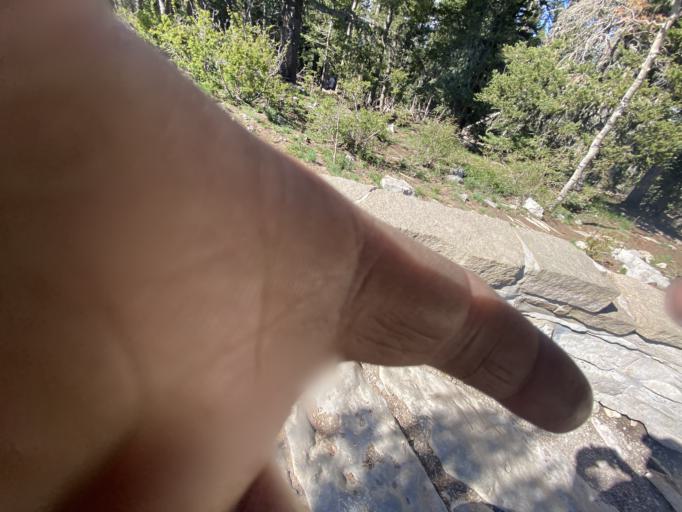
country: US
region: New Mexico
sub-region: Bernalillo County
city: Sandia Heights
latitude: 35.2070
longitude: -106.4467
